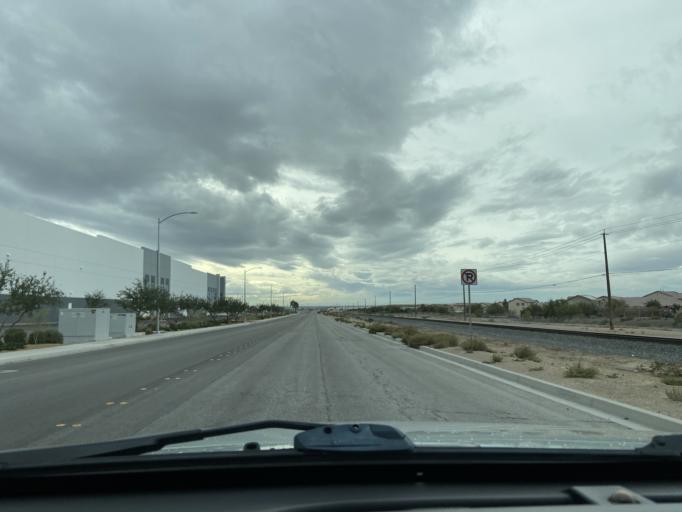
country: US
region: Nevada
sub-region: Clark County
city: Nellis Air Force Base
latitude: 36.2605
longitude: -115.0854
